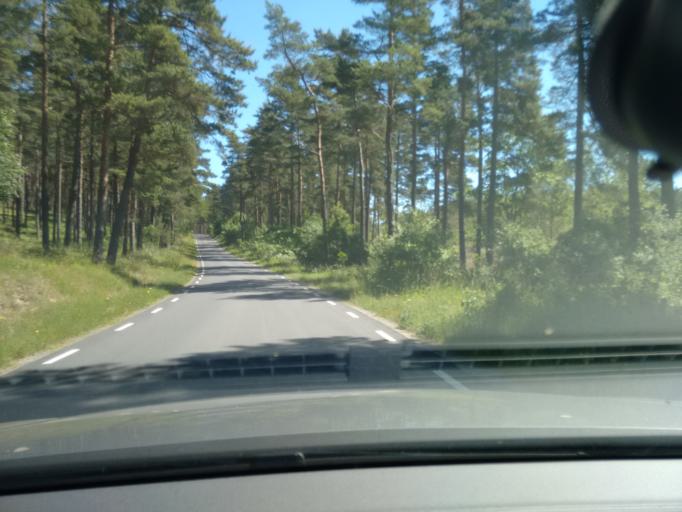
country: SE
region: Skane
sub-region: Kristianstads Kommun
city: Degeberga
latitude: 55.7731
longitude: 14.1278
